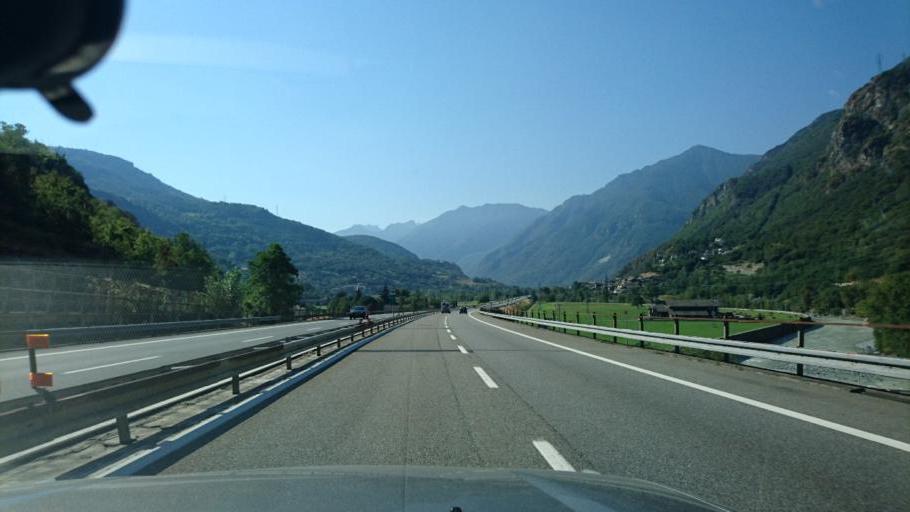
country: IT
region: Aosta Valley
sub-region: Valle d'Aosta
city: Montjovet
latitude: 45.7189
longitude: 7.6703
